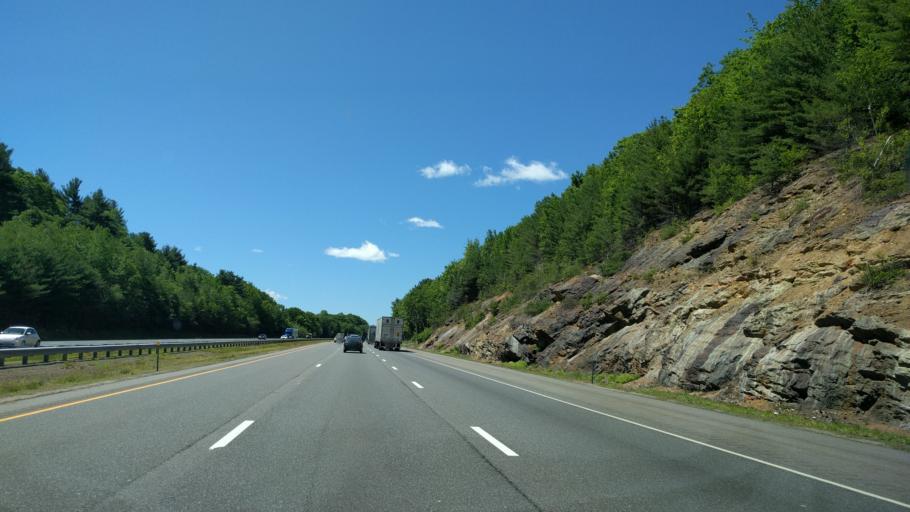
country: US
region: Massachusetts
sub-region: Hampden County
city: Holland
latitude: 42.0002
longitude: -72.1655
